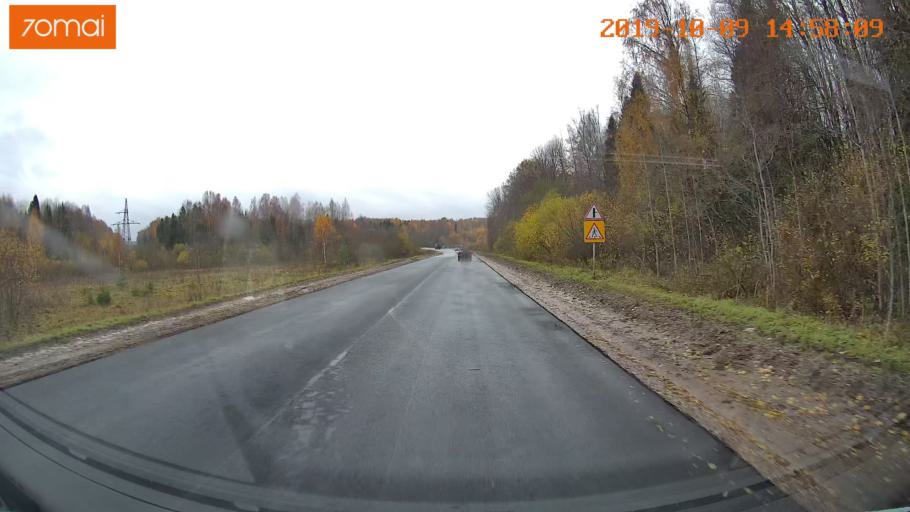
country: RU
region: Kostroma
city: Chistyye Bory
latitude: 58.3298
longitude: 41.6537
